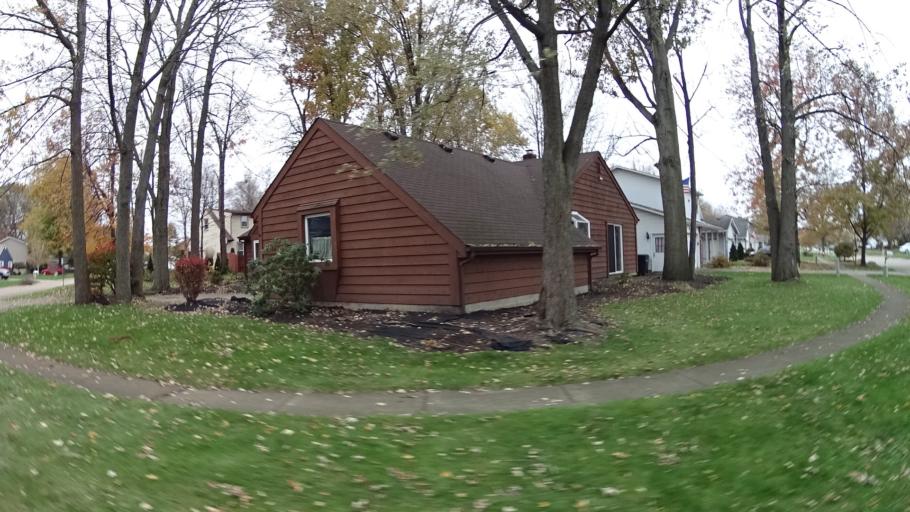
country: US
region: Ohio
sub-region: Lorain County
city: Sheffield
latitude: 41.4174
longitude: -82.0870
